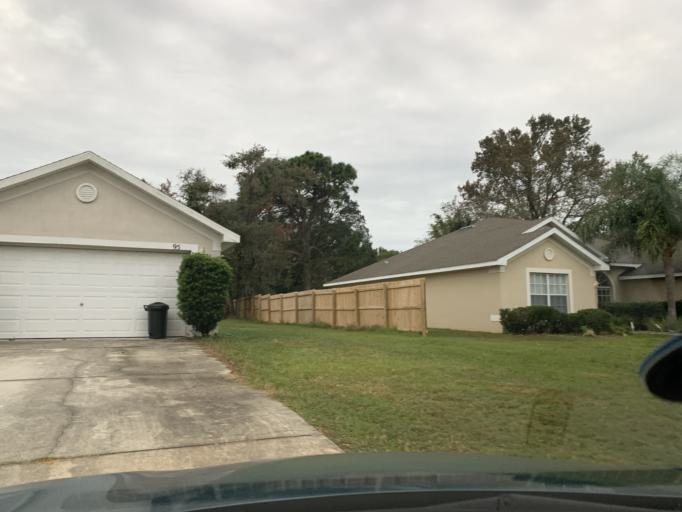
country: US
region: Florida
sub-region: Hernando County
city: Timber Pines
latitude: 28.4343
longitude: -82.5806
